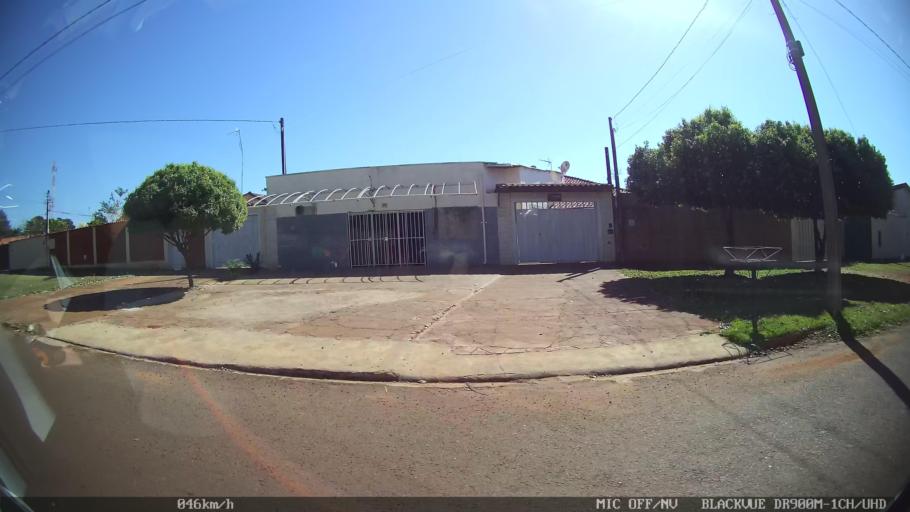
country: BR
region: Sao Paulo
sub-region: Batatais
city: Batatais
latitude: -20.8848
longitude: -47.5678
